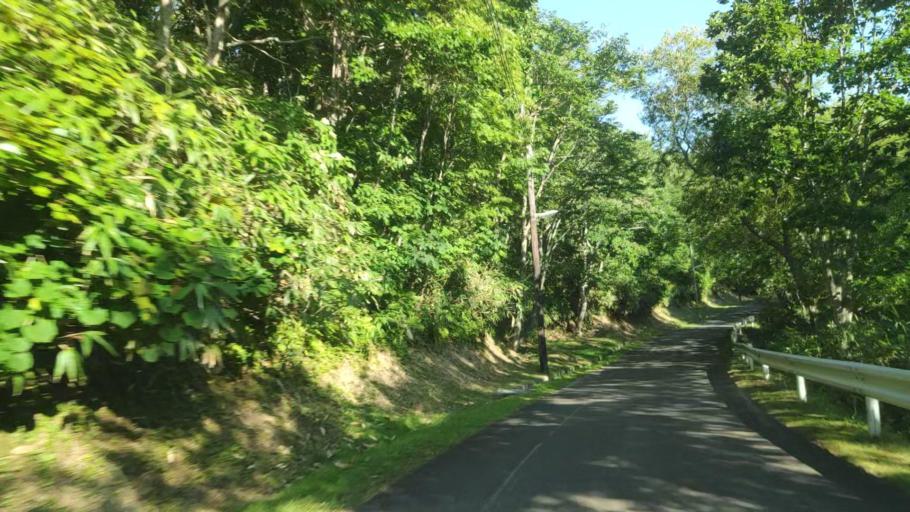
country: JP
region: Hokkaido
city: Wakkanai
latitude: 45.4145
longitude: 141.6677
